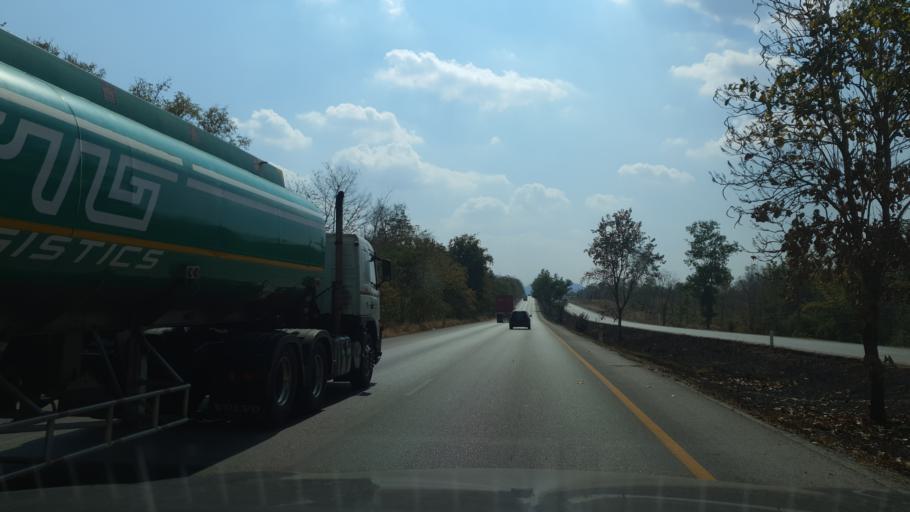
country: TH
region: Lampang
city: Mae Phrik
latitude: 17.3941
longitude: 99.1491
